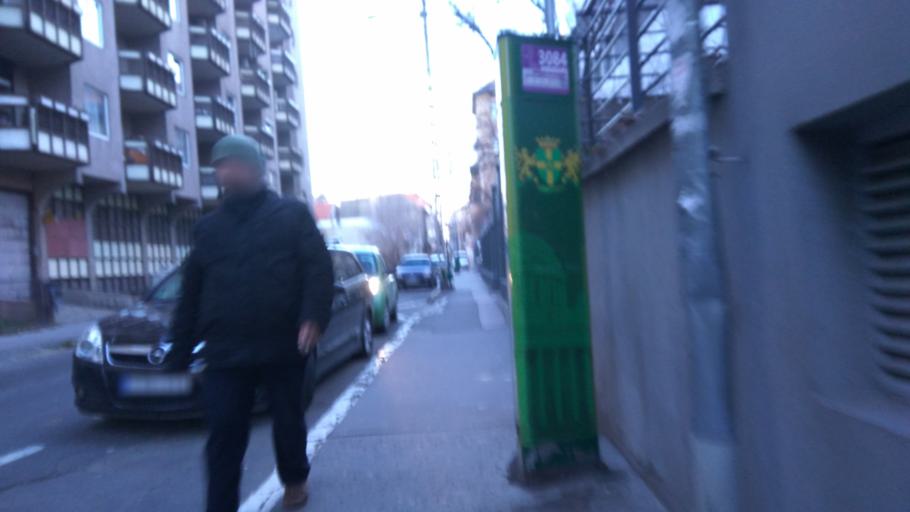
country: HU
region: Budapest
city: Budapest VIII. keruelet
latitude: 47.4926
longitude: 19.0771
